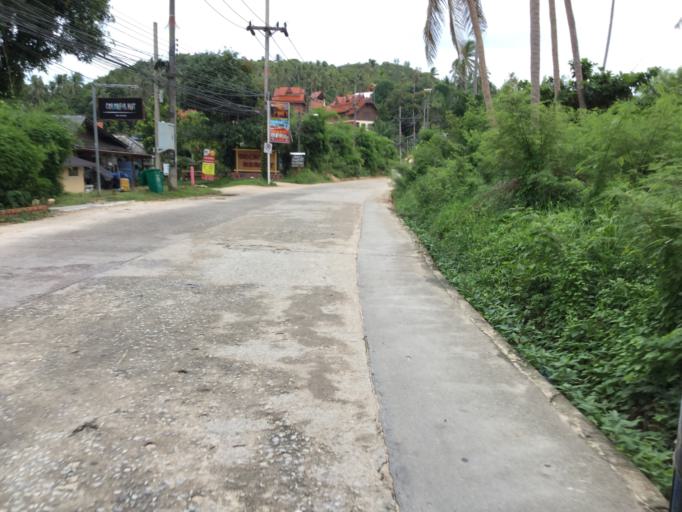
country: TH
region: Surat Thani
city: Ko Pha-Ngan
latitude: 9.7192
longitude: 99.9823
